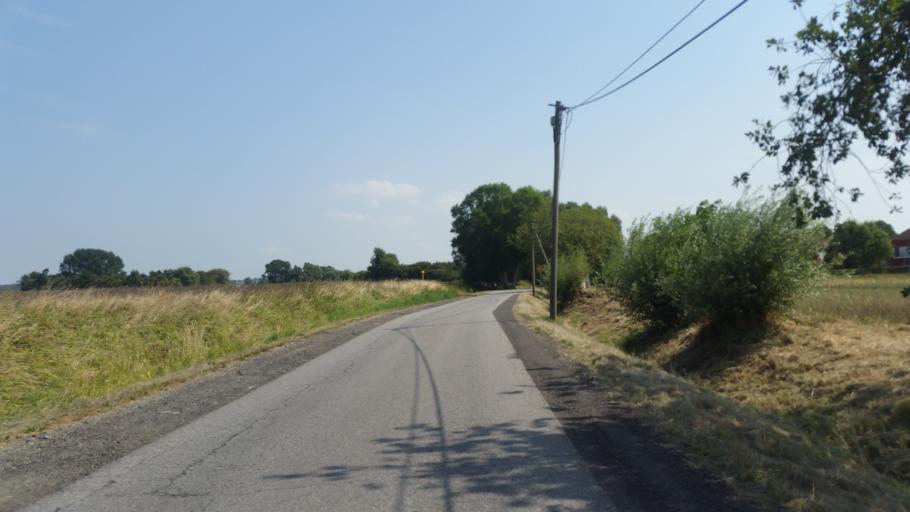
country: DE
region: Mecklenburg-Vorpommern
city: Biendorf
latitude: 54.0945
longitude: 11.6407
